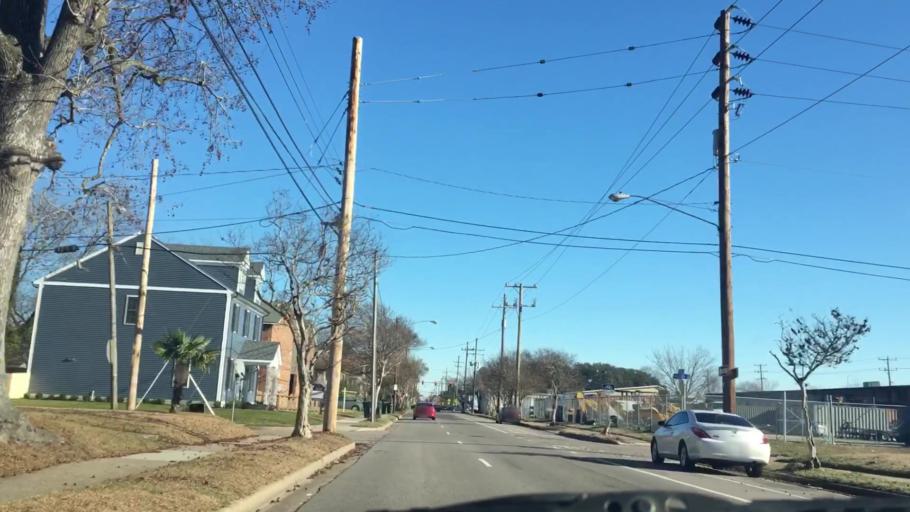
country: US
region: Virginia
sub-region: City of Norfolk
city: Norfolk
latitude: 36.8751
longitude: -76.2974
